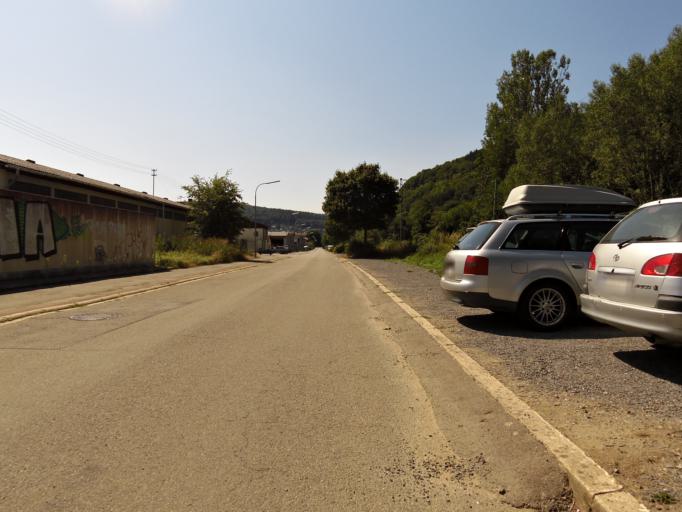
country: DE
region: Baden-Wuerttemberg
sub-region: Karlsruhe Region
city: Mosbach
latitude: 49.3649
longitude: 9.1481
